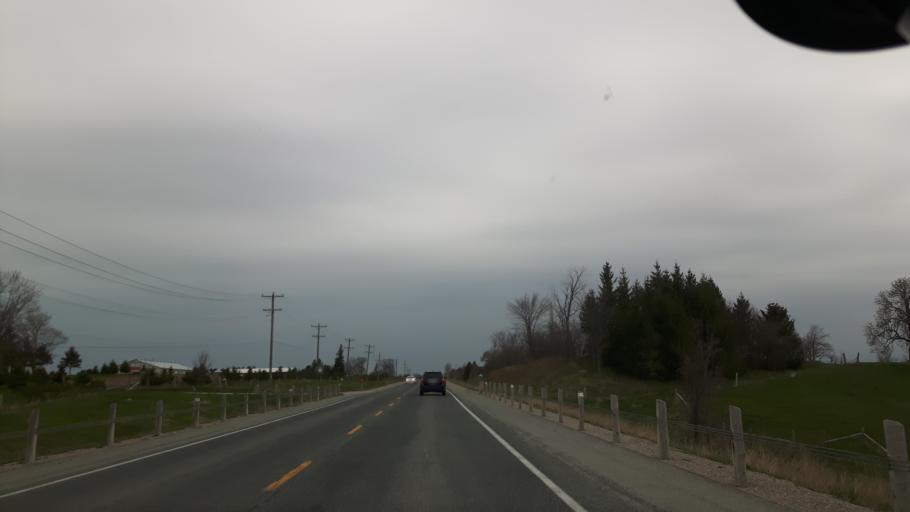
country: CA
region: Ontario
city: Goderich
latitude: 43.6803
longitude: -81.6281
